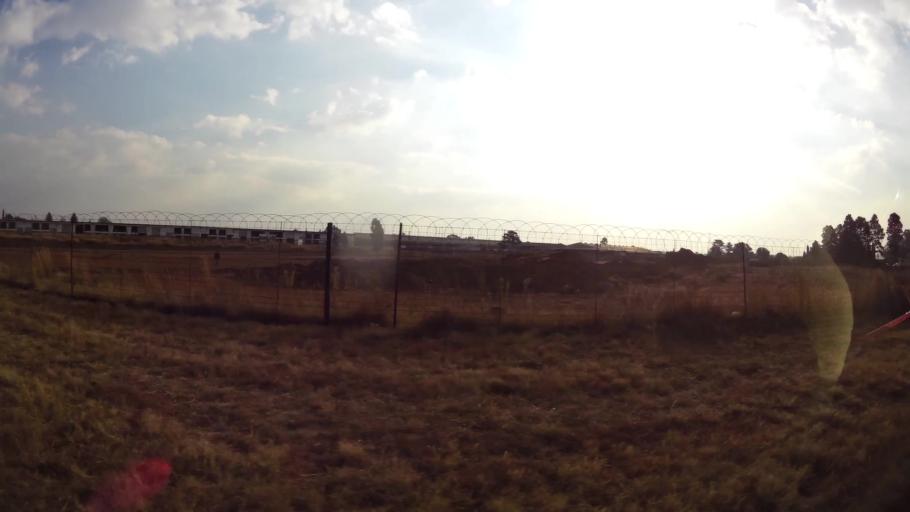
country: ZA
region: Gauteng
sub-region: Ekurhuleni Metropolitan Municipality
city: Benoni
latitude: -26.1119
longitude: 28.2743
